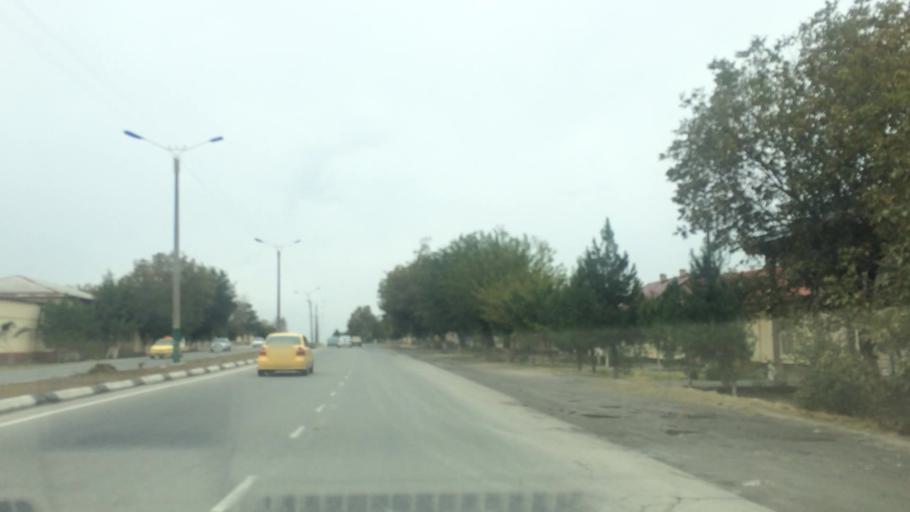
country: UZ
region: Samarqand
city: Bulung'ur
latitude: 39.7682
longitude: 67.2622
